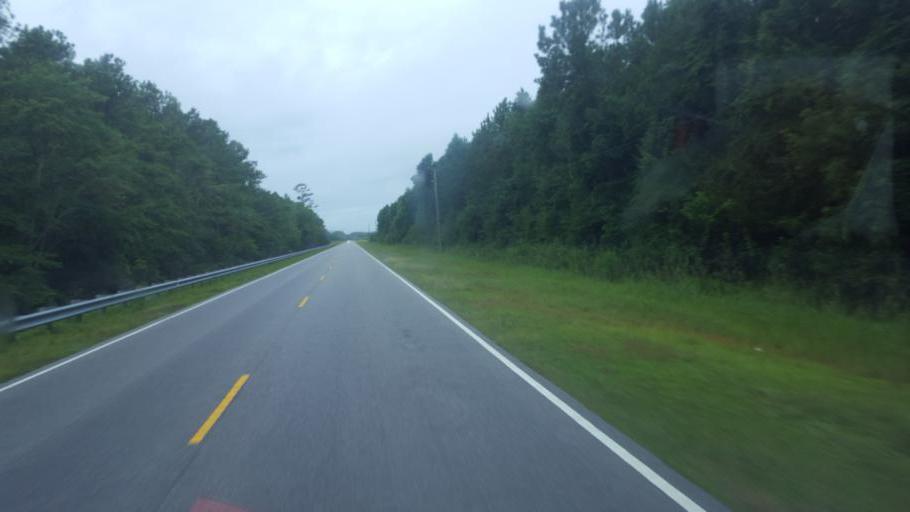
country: US
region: North Carolina
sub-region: Tyrrell County
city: Columbia
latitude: 35.9027
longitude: -76.0879
